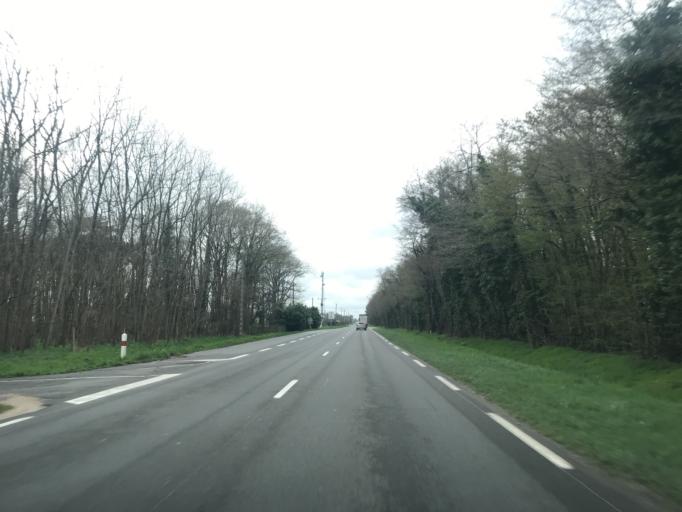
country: FR
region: Centre
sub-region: Departement du Loiret
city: Bray-en-Val
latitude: 47.8411
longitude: 2.3334
